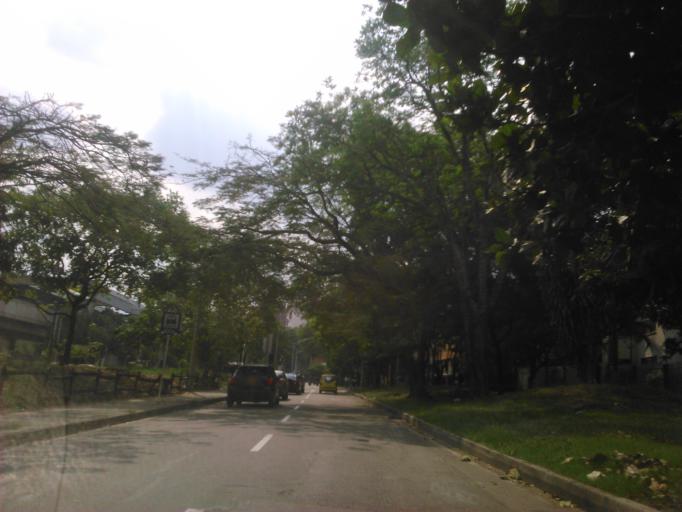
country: CO
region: Antioquia
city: Medellin
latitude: 6.2531
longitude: -75.5815
